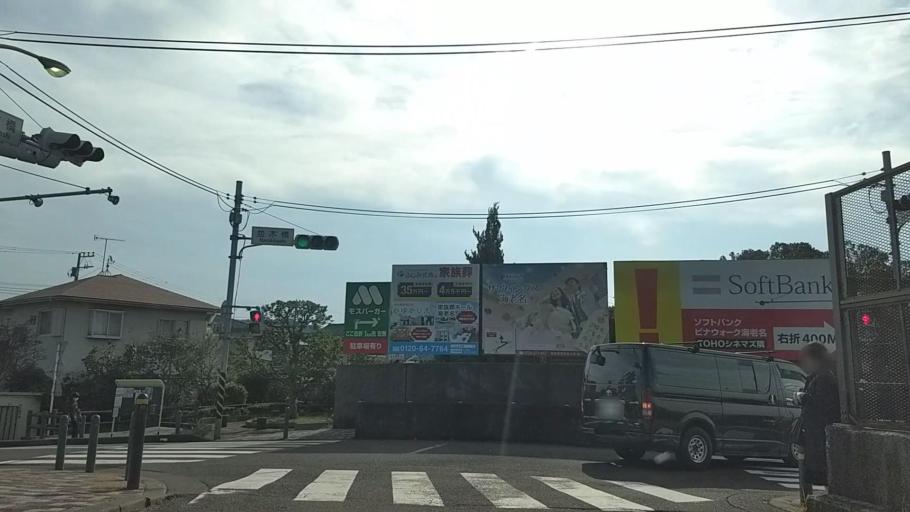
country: JP
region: Kanagawa
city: Zama
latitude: 35.4569
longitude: 139.3956
